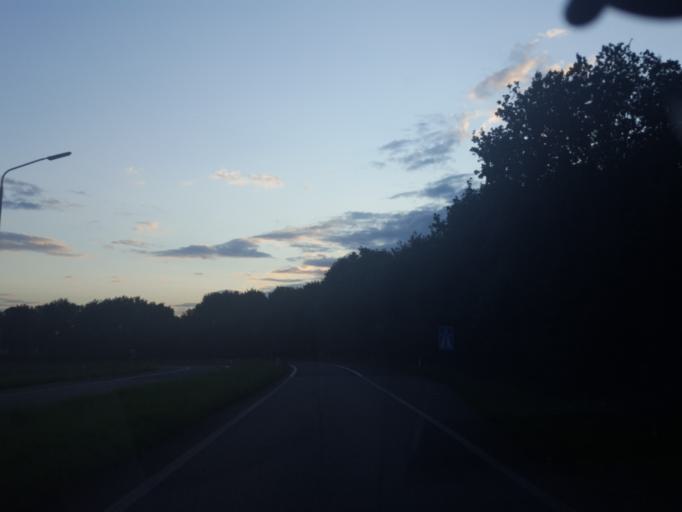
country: NL
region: Gelderland
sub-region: Gemeente Wijchen
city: Wijchen
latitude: 51.8286
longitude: 5.7367
